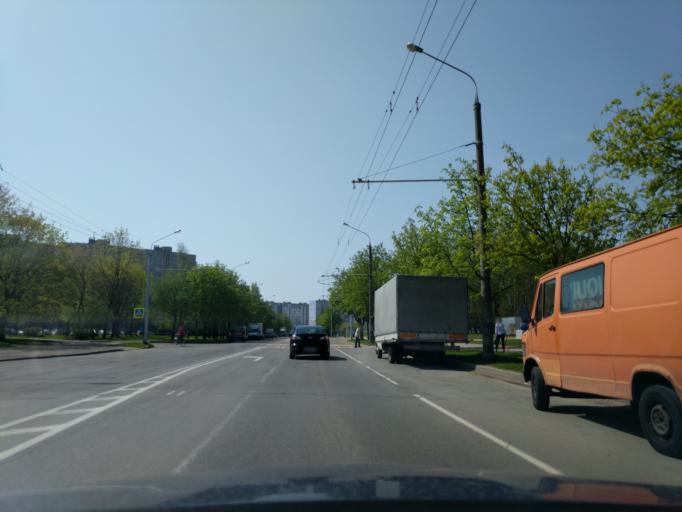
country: BY
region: Minsk
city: Novoye Medvezhino
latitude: 53.8677
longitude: 27.4572
